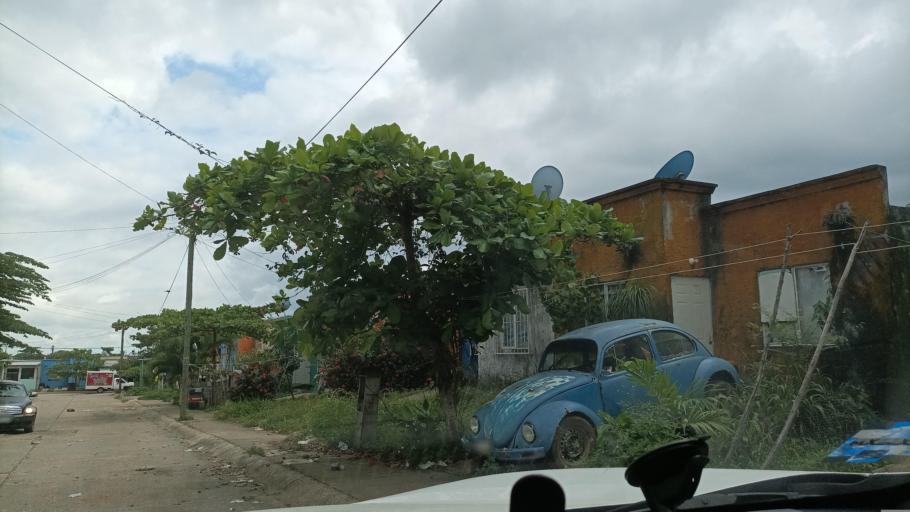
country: MX
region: Veracruz
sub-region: Soconusco
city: Fraccionamiento Santa Cruz
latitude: 17.9719
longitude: -94.8980
